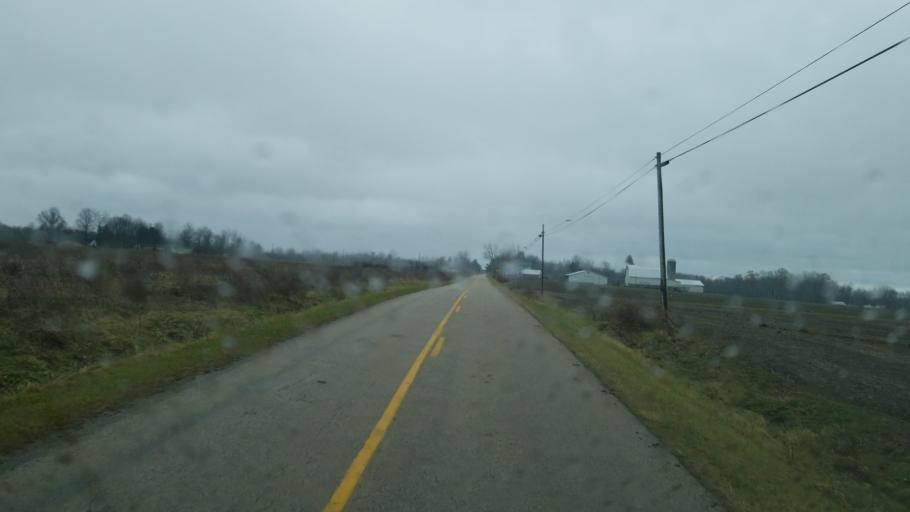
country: US
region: Ohio
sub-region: Ashtabula County
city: Roaming Shores
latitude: 41.6095
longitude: -80.7630
